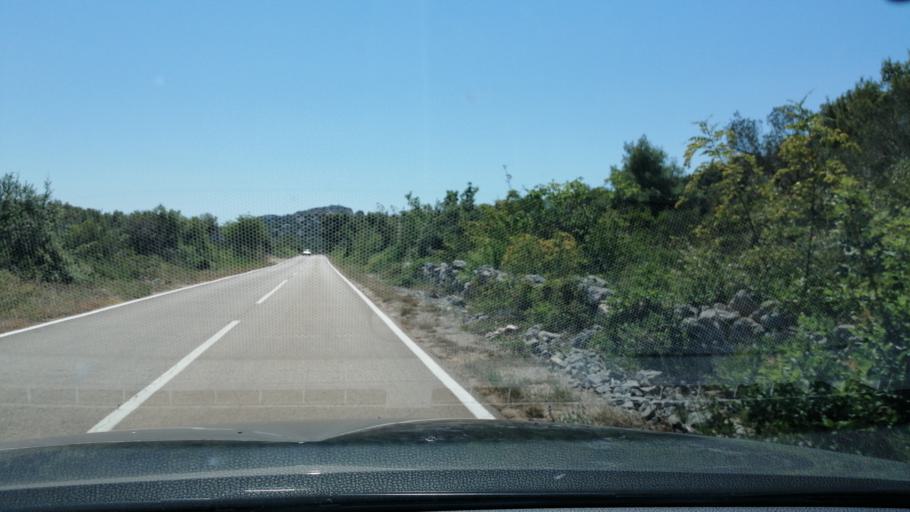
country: HR
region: Sibensko-Kniniska
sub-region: Grad Sibenik
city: Pirovac
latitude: 43.8431
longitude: 15.6877
